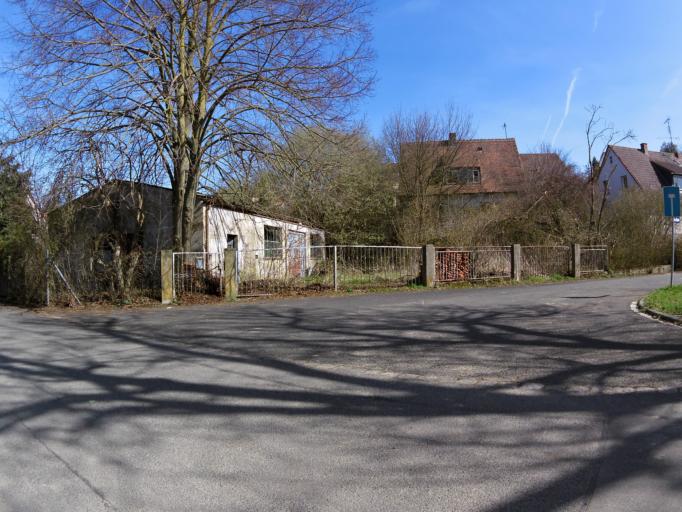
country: DE
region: Bavaria
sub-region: Regierungsbezirk Unterfranken
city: Biebelried
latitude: 49.7970
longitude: 10.1082
